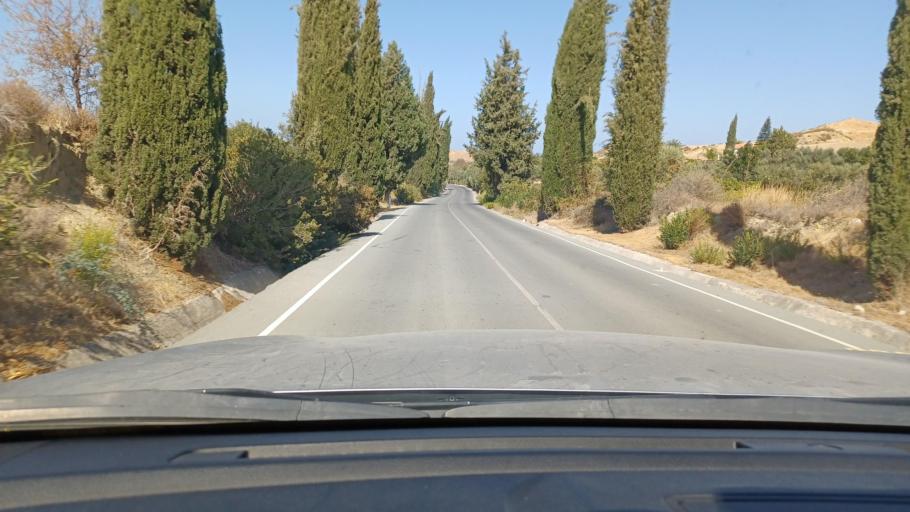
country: CY
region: Pafos
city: Polis
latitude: 35.0137
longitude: 32.4510
